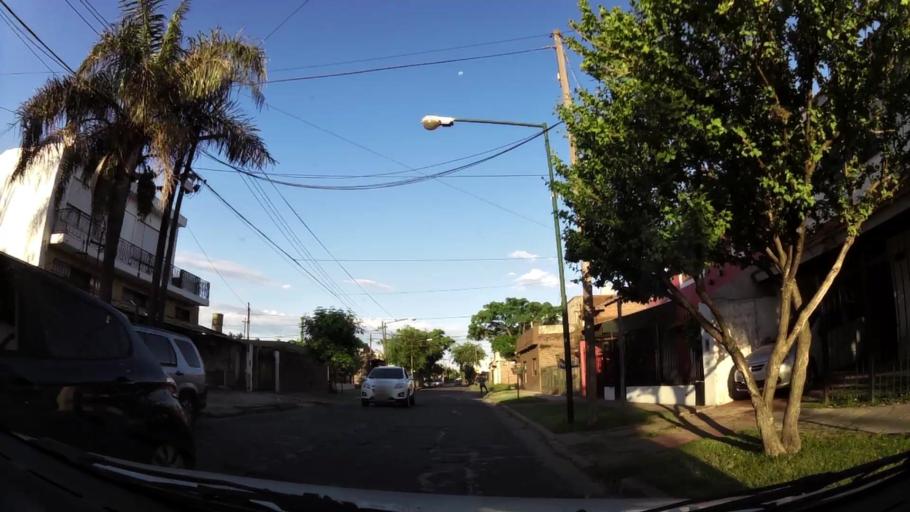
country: AR
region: Buenos Aires
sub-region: Partido de San Isidro
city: San Isidro
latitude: -34.4686
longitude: -58.5482
